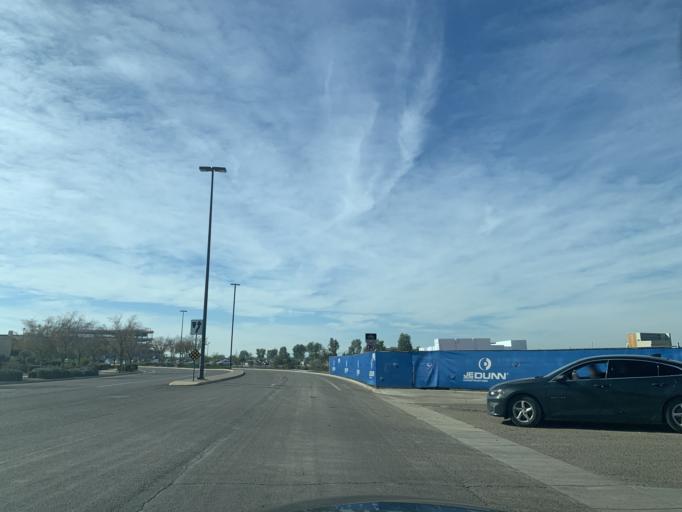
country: US
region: Arizona
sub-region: Maricopa County
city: Gilbert
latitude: 33.2916
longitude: -111.7468
